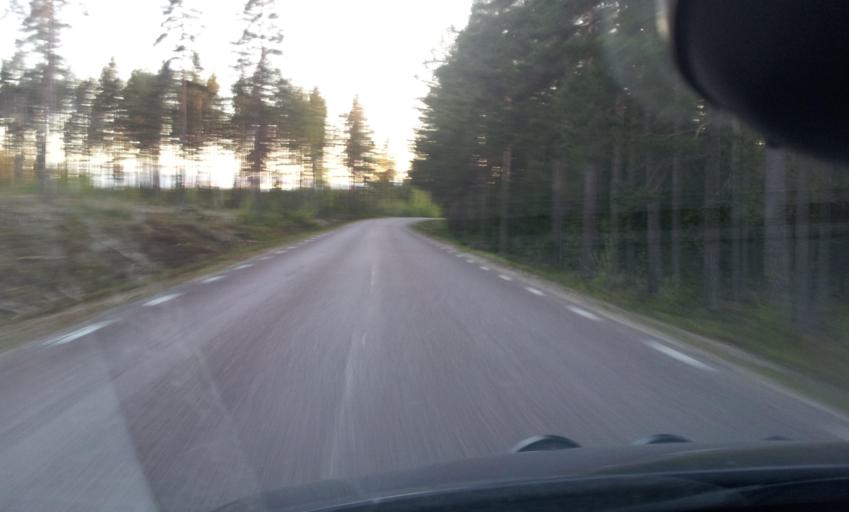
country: SE
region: Gaevleborg
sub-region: Bollnas Kommun
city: Bollnas
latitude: 61.3921
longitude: 16.4524
